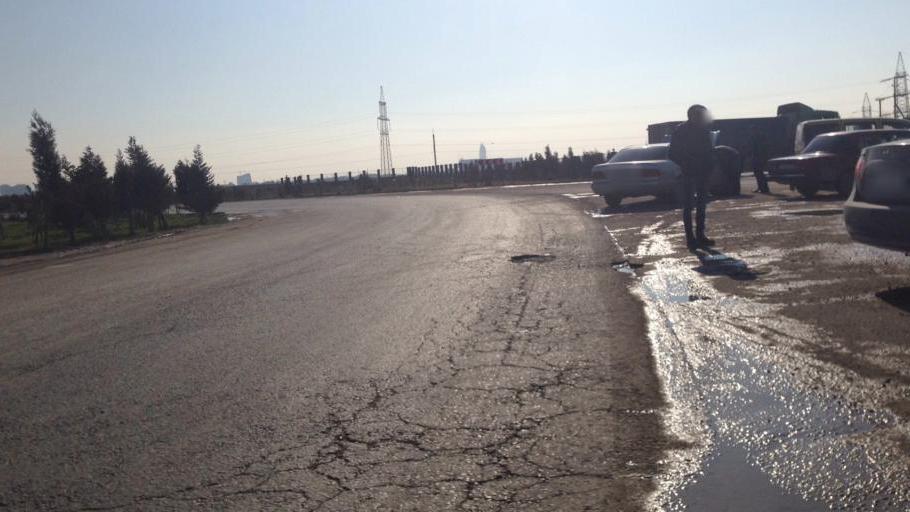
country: AZ
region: Baki
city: Balakhani
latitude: 40.4540
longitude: 49.8934
